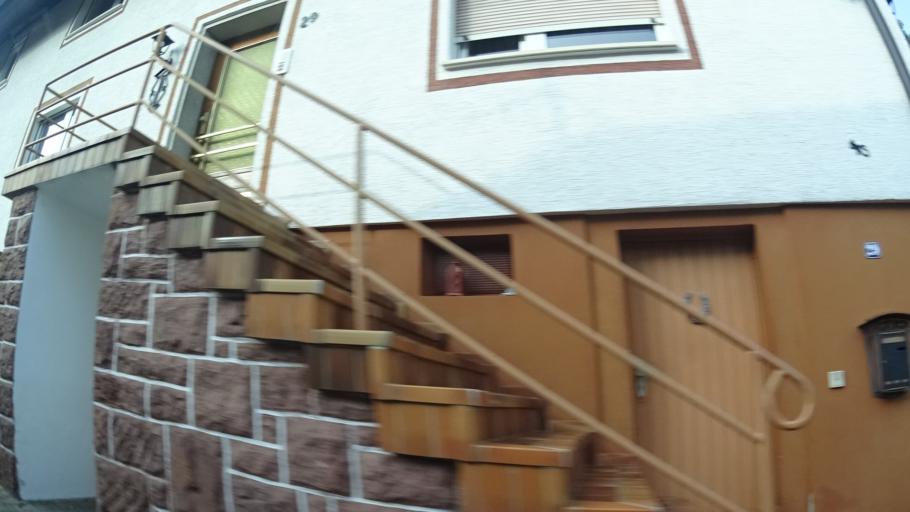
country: DE
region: Hesse
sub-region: Regierungsbezirk Darmstadt
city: Rothenberg
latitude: 49.5490
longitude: 8.9019
